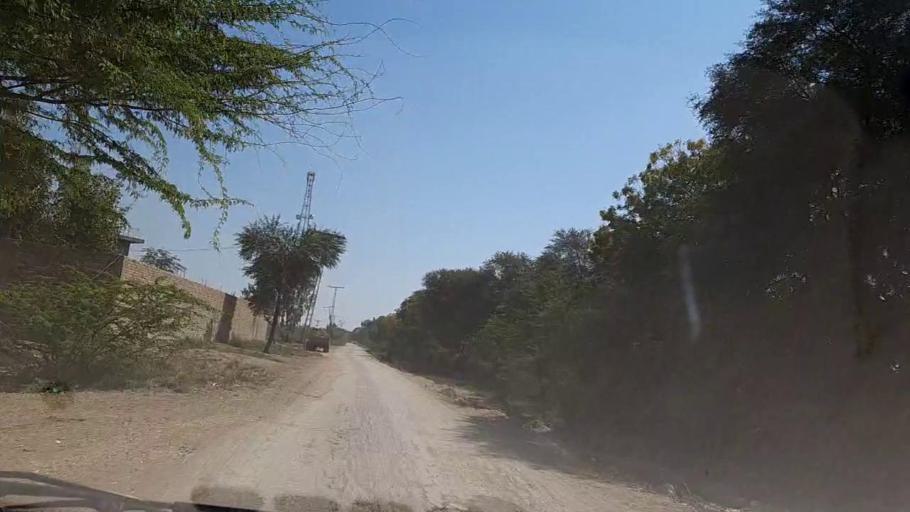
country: PK
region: Sindh
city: Mirpur Khas
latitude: 25.4335
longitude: 69.0172
